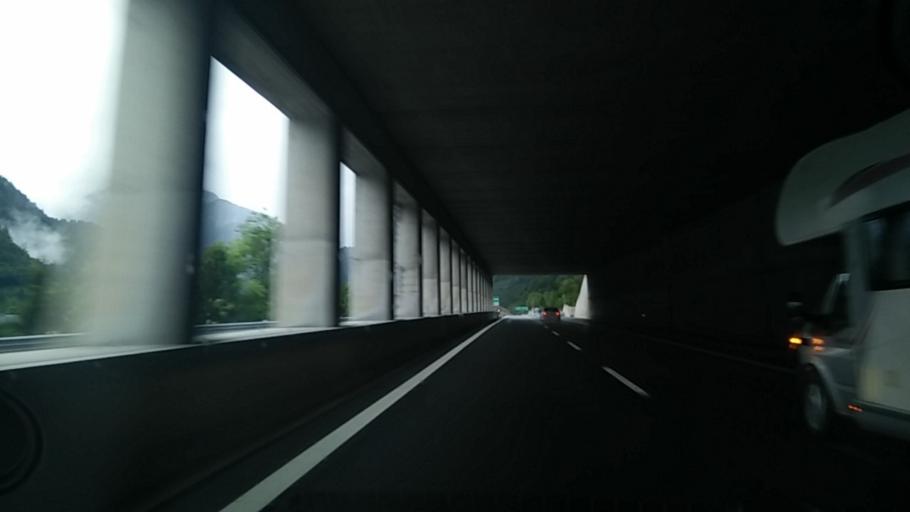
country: IT
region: Friuli Venezia Giulia
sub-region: Provincia di Udine
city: Pontebba
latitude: 46.5123
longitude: 13.3411
